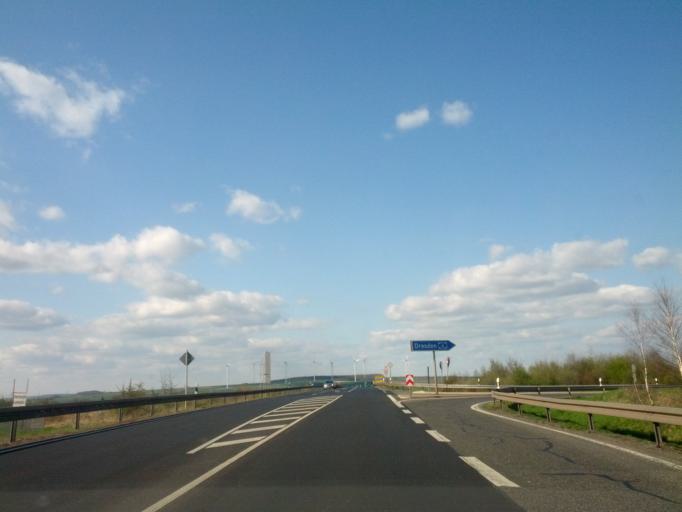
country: DE
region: Thuringia
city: Waltershausen
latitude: 50.9180
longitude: 10.5484
